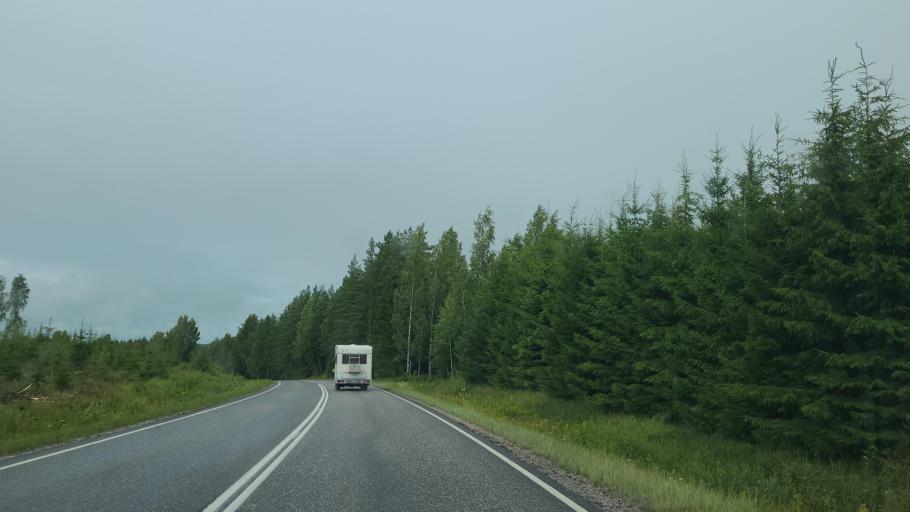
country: FI
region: Varsinais-Suomi
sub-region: Turku
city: Sauvo
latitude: 60.3054
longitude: 22.6863
